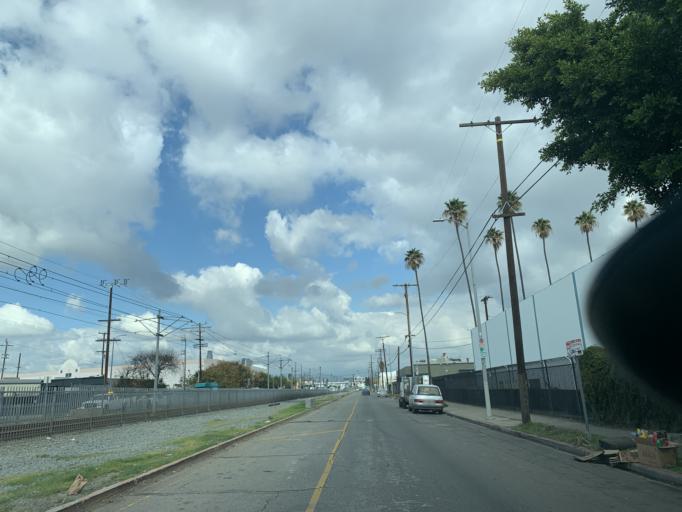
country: US
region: California
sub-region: Los Angeles County
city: Los Angeles
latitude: 34.0160
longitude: -118.2429
